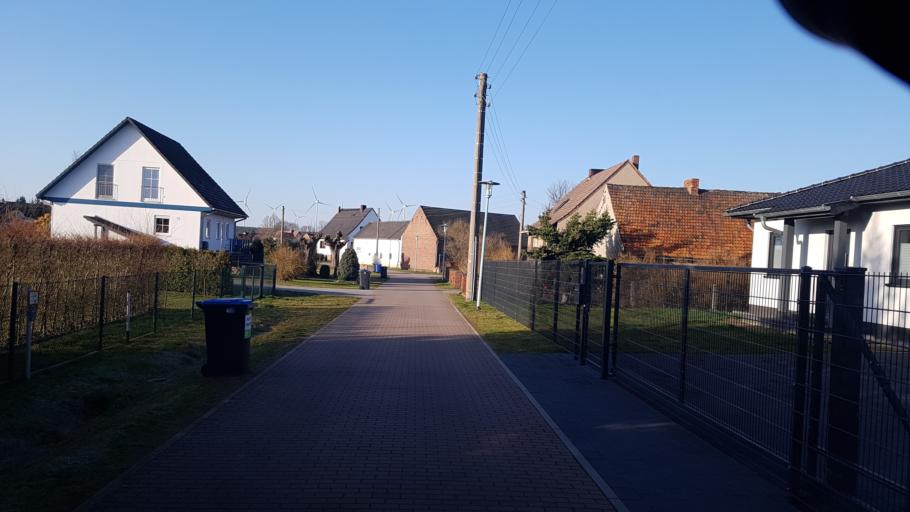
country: DE
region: Brandenburg
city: Calau
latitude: 51.7639
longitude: 13.9141
